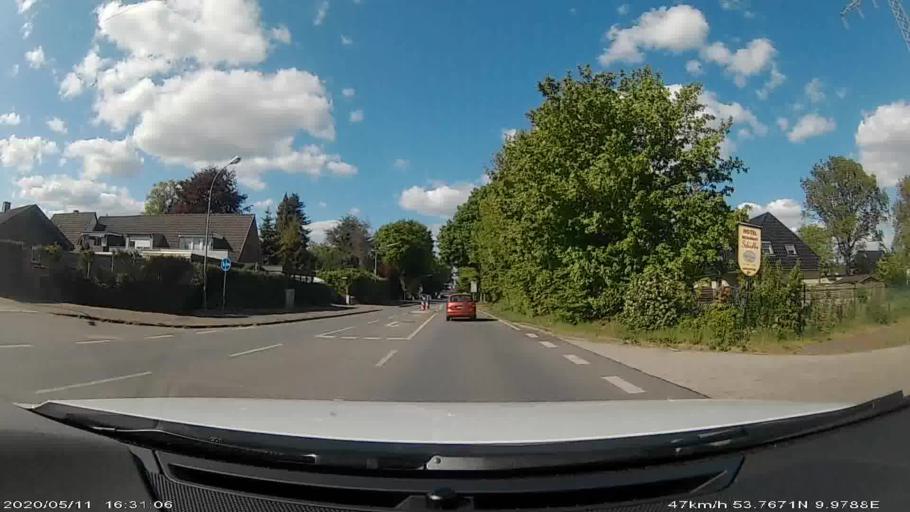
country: DE
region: Schleswig-Holstein
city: Henstedt-Ulzburg
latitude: 53.7710
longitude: 9.9842
